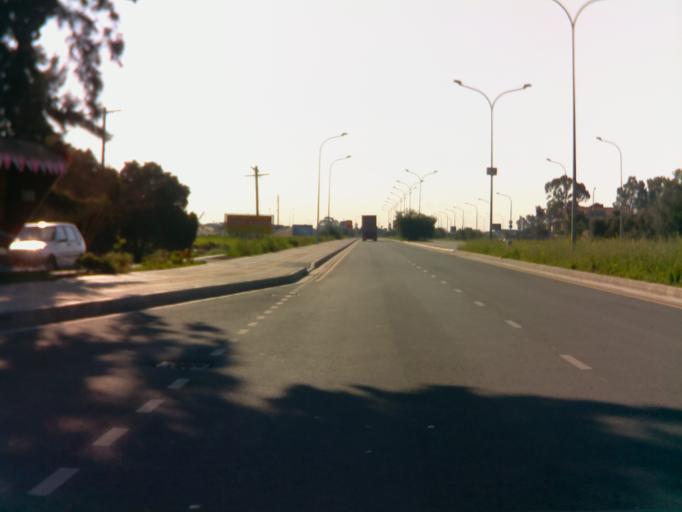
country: CY
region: Limassol
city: Limassol
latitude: 34.6499
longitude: 32.9999
